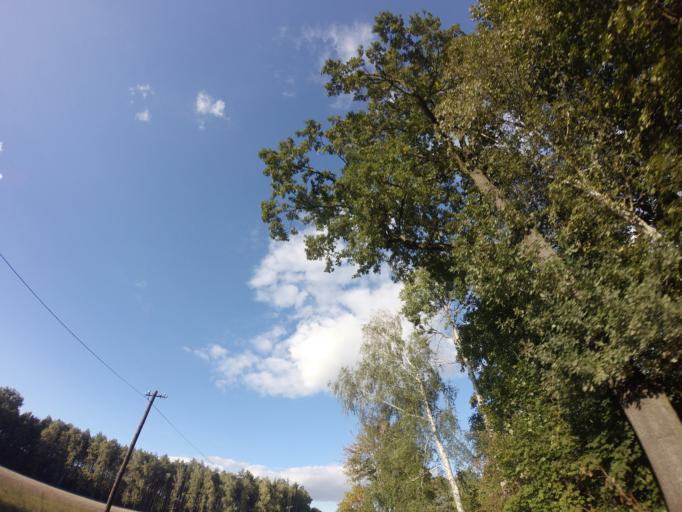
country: PL
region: Greater Poland Voivodeship
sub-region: Powiat nowotomyski
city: Nowy Tomysl
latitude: 52.2815
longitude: 16.1261
